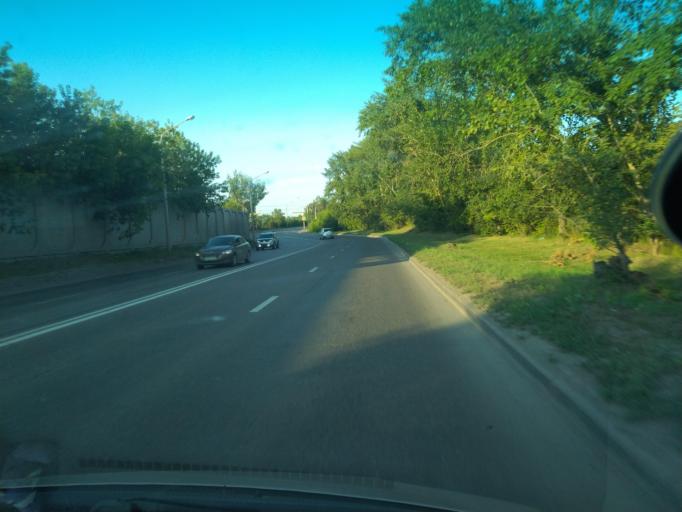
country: RU
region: Krasnoyarskiy
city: Berezovka
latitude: 56.0150
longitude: 93.0253
